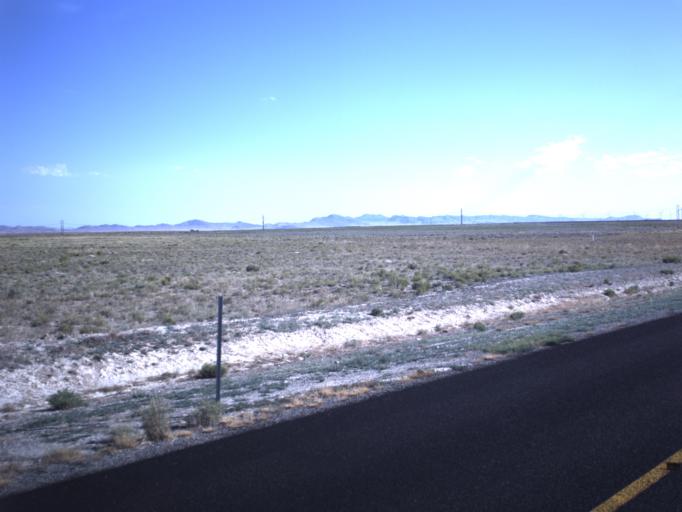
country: US
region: Utah
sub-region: Beaver County
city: Milford
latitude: 38.4734
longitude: -112.9931
